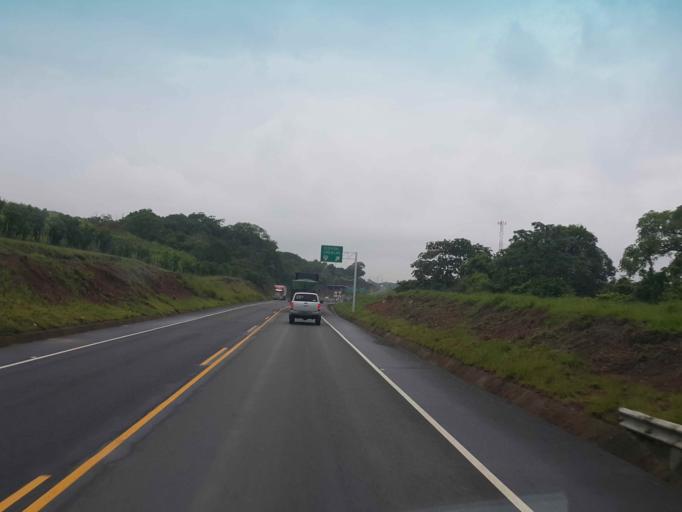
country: CR
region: Alajuela
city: Carrillos
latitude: 9.9644
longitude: -84.2873
